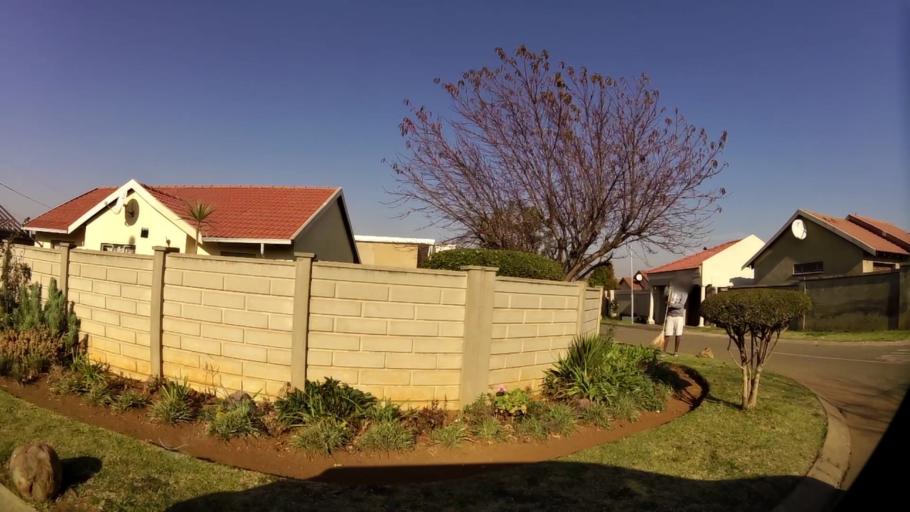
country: ZA
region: Gauteng
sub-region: City of Johannesburg Metropolitan Municipality
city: Soweto
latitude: -26.2924
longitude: 27.9491
